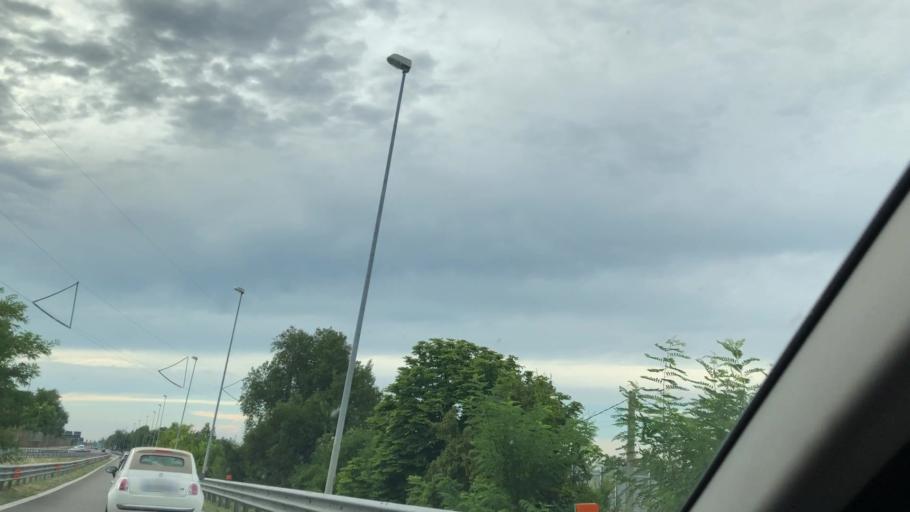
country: IT
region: Emilia-Romagna
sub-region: Provincia di Bologna
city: Calderara di Reno
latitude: 44.5203
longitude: 11.2810
